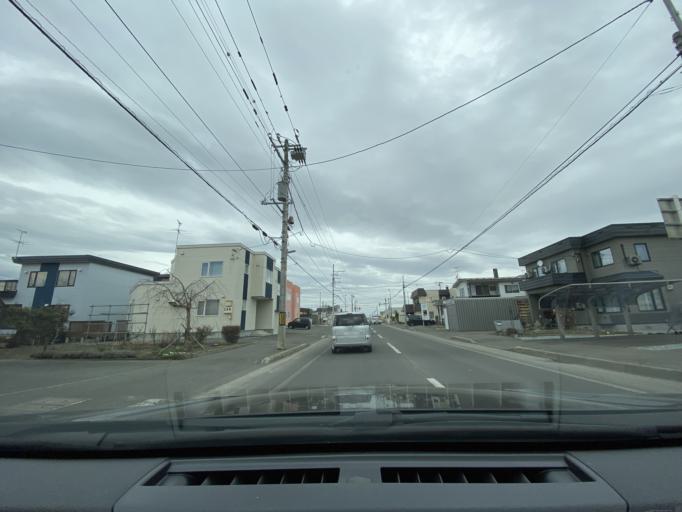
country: JP
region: Hokkaido
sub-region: Asahikawa-shi
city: Asahikawa
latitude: 43.7893
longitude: 142.4135
